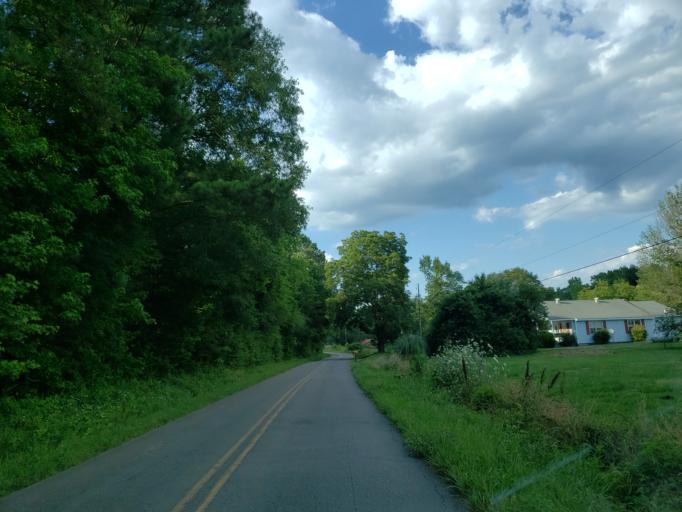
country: US
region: Georgia
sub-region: Haralson County
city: Buchanan
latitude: 33.9132
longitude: -85.2731
